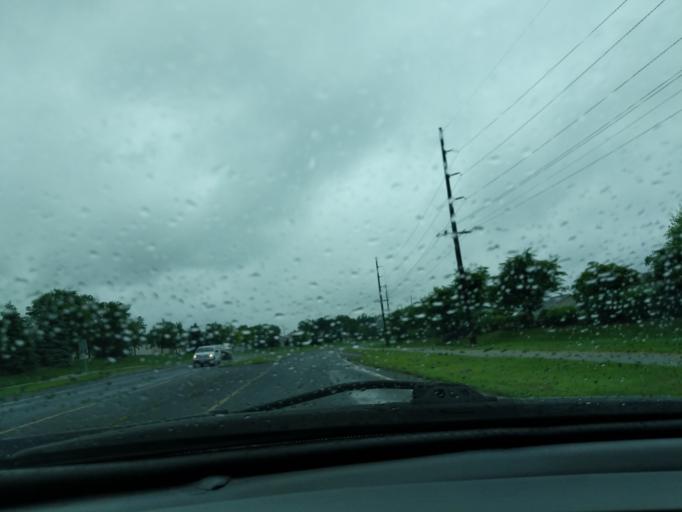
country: US
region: Indiana
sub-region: Hamilton County
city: Noblesville
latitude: 40.0620
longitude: -86.0335
